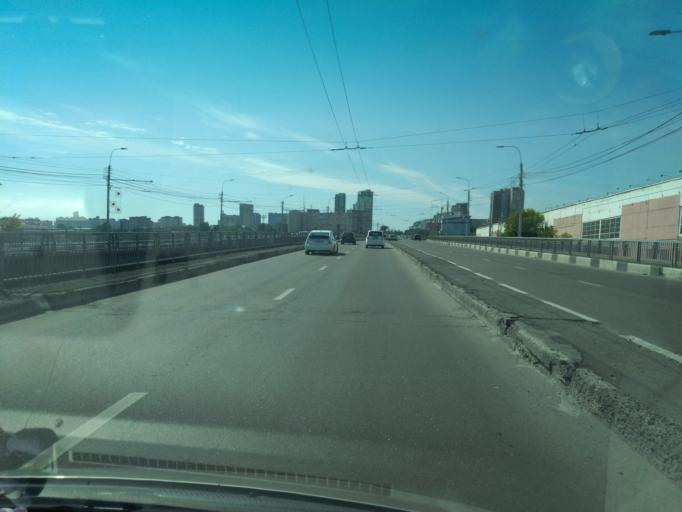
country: RU
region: Krasnoyarskiy
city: Krasnoyarsk
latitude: 56.0125
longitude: 92.8356
